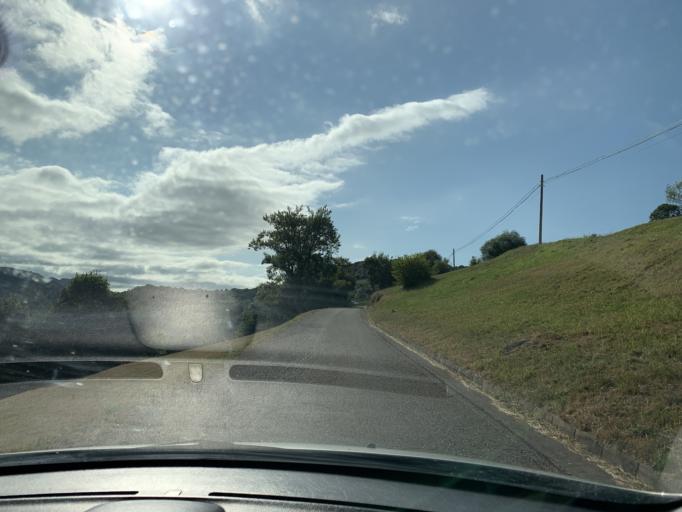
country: ES
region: Asturias
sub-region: Province of Asturias
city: Carrena
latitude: 43.3189
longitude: -4.8515
